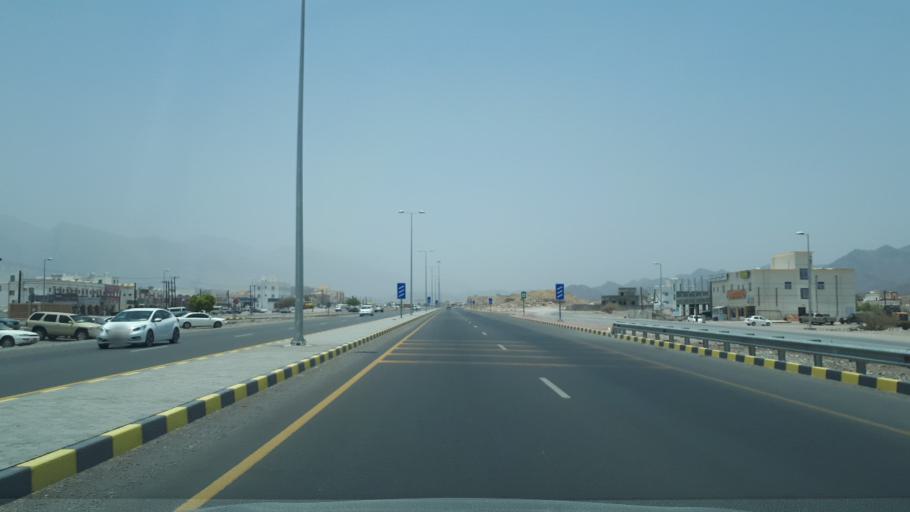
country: OM
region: Al Batinah
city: Rustaq
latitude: 23.4361
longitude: 57.3930
